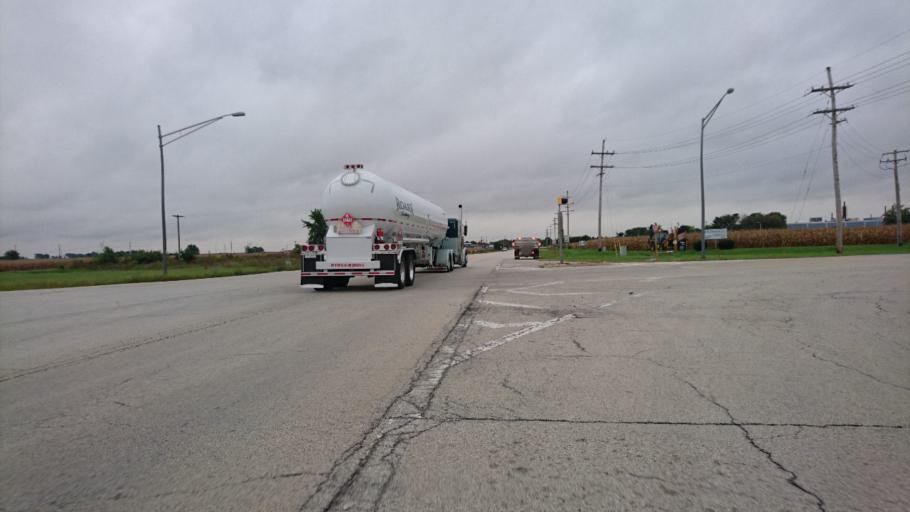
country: US
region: Illinois
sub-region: Livingston County
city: Dwight
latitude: 41.1099
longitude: -88.4137
